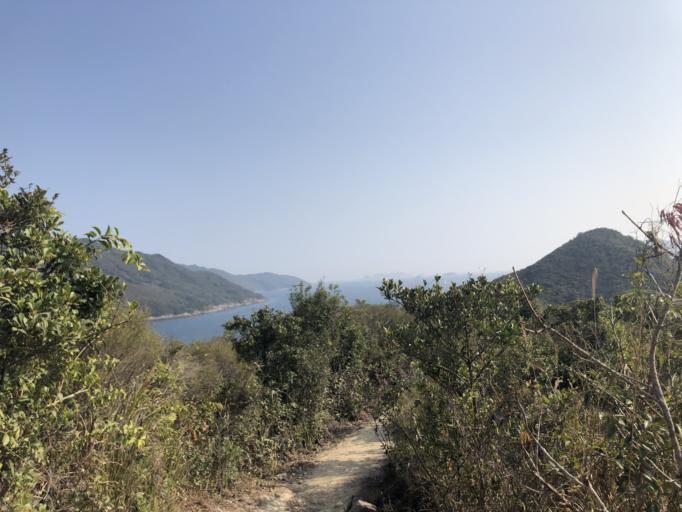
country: HK
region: Sai Kung
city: Sai Kung
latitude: 22.3588
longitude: 114.2954
